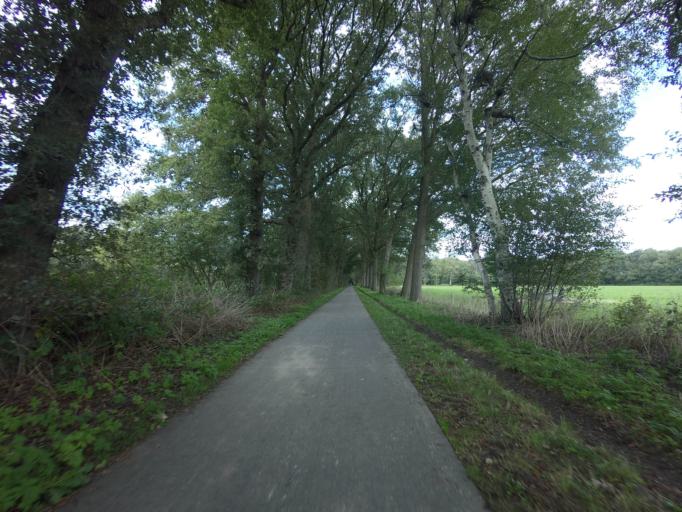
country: NL
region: Drenthe
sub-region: Gemeente De Wolden
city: Ruinen
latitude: 52.8012
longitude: 6.3478
